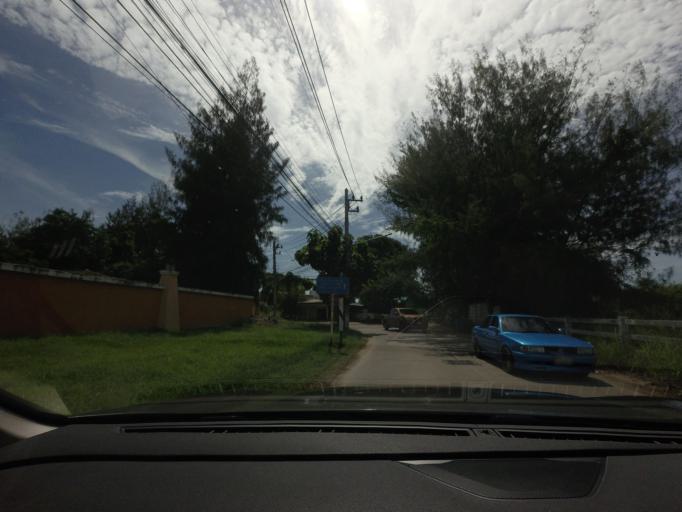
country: TH
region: Prachuap Khiri Khan
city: Hua Hin
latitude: 12.5136
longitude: 99.9713
